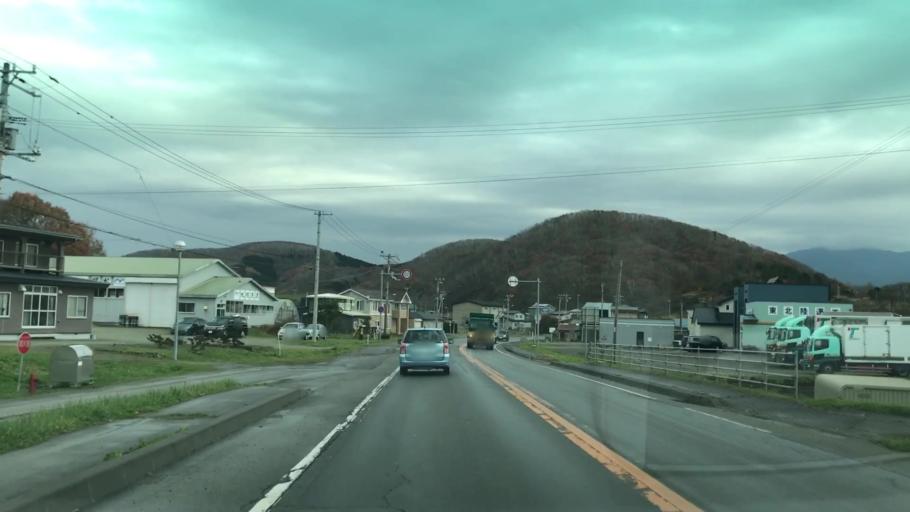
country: JP
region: Hokkaido
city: Shizunai-furukawacho
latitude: 42.1338
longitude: 142.9049
